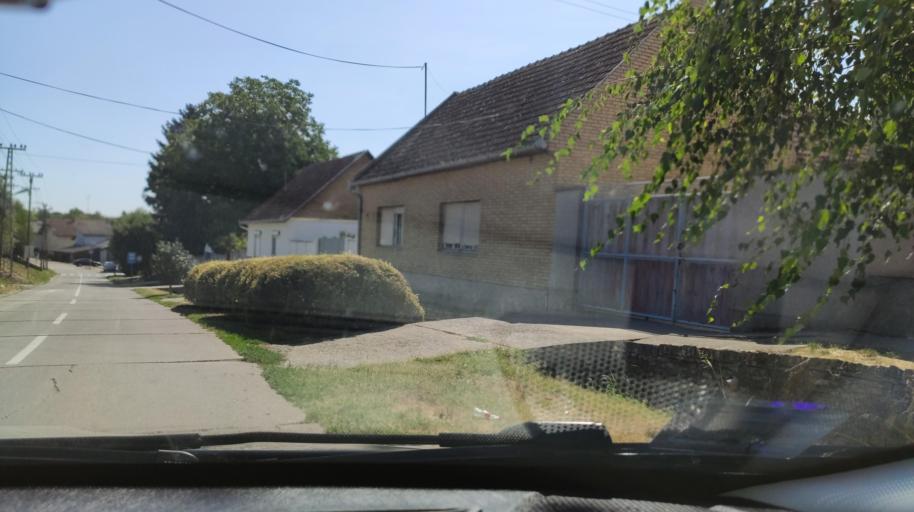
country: RS
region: Autonomna Pokrajina Vojvodina
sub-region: Severnobacki Okrug
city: Backa Topola
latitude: 45.8189
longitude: 19.6245
